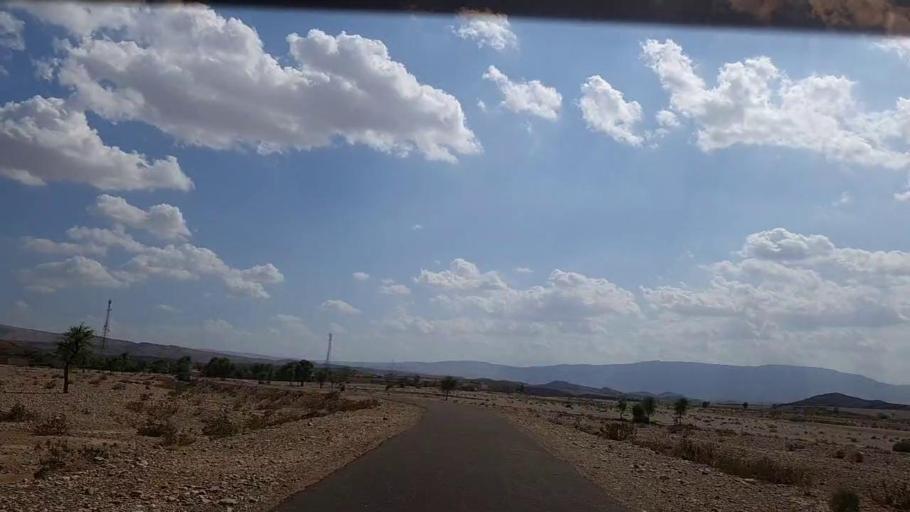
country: PK
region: Sindh
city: Johi
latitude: 26.5013
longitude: 67.4365
